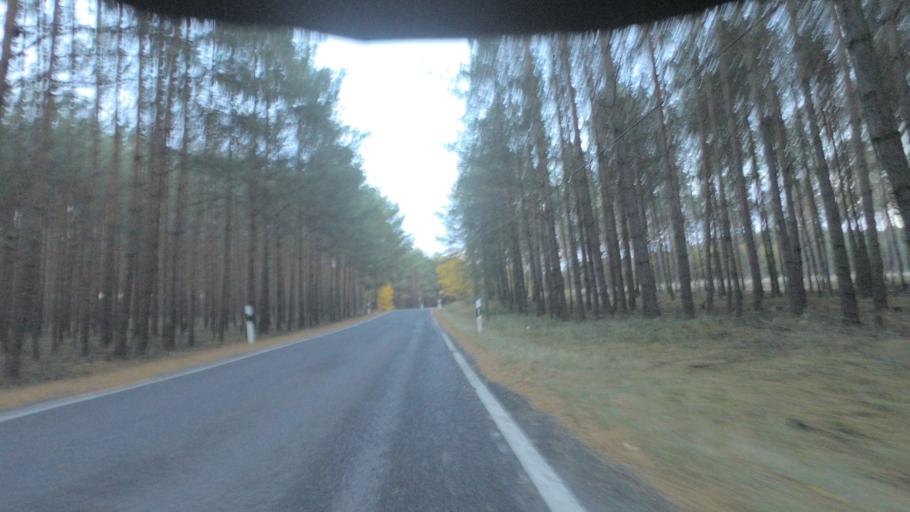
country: DE
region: Brandenburg
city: Schonewalde
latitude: 51.7566
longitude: 13.6037
